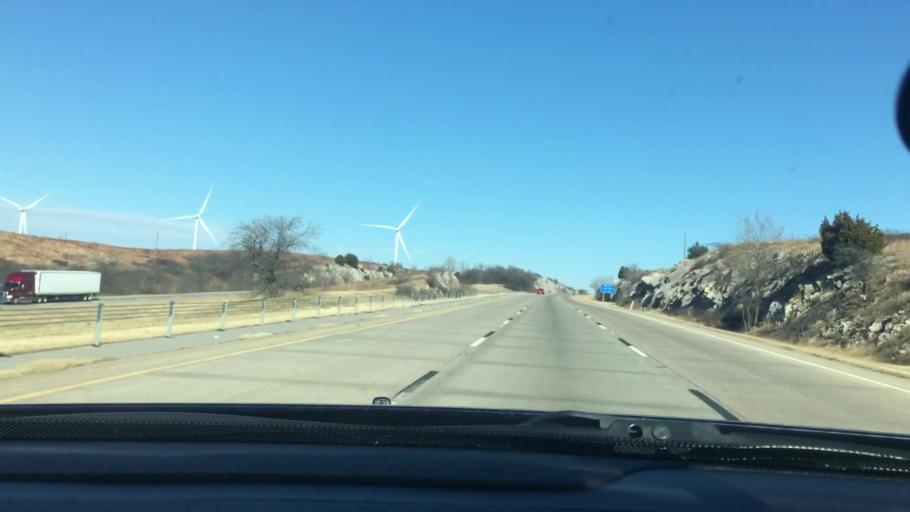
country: US
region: Oklahoma
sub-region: Murray County
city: Davis
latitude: 34.3681
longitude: -97.1460
